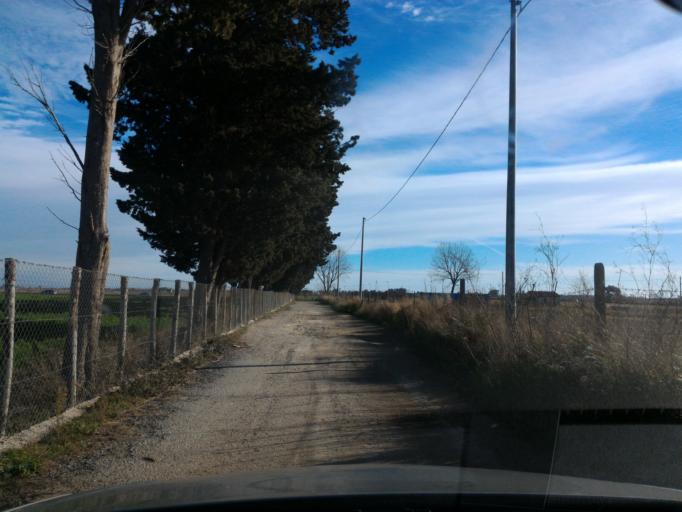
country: IT
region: Calabria
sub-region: Provincia di Crotone
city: Isola di Capo Rizzuto
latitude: 38.9876
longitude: 17.0750
